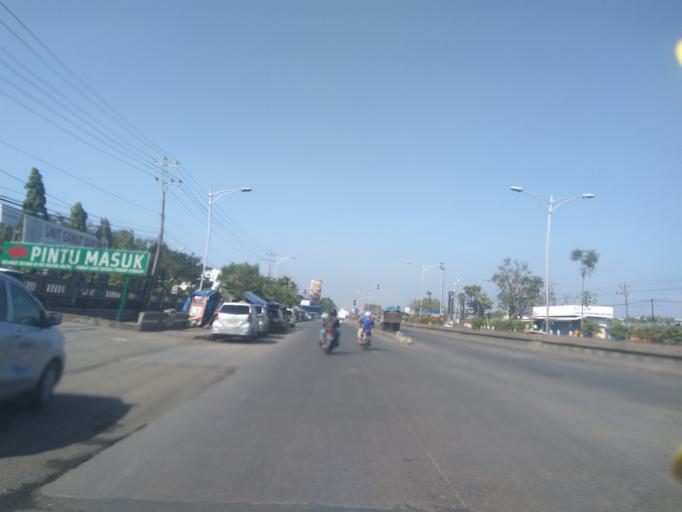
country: ID
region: Central Java
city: Semarang
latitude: -6.9561
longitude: 110.4617
